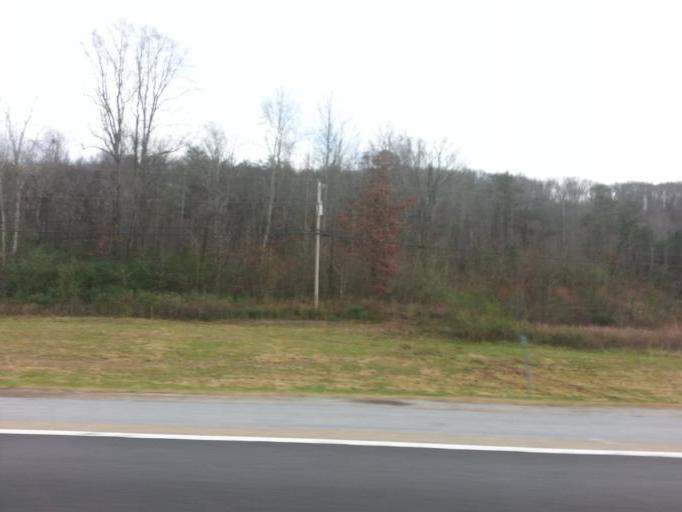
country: US
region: Tennessee
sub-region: Rhea County
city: Graysville
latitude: 35.4504
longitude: -85.0574
